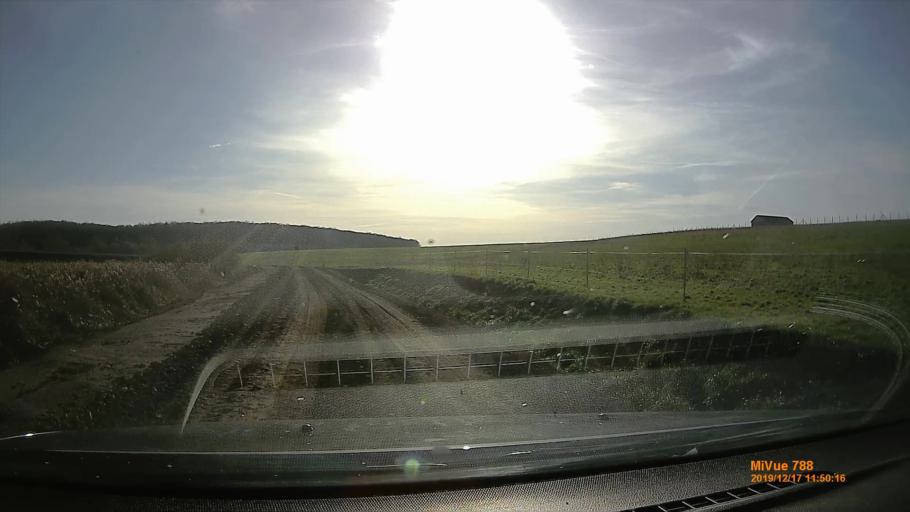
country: HU
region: Somogy
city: Kaposvar
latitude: 46.4536
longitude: 17.7687
